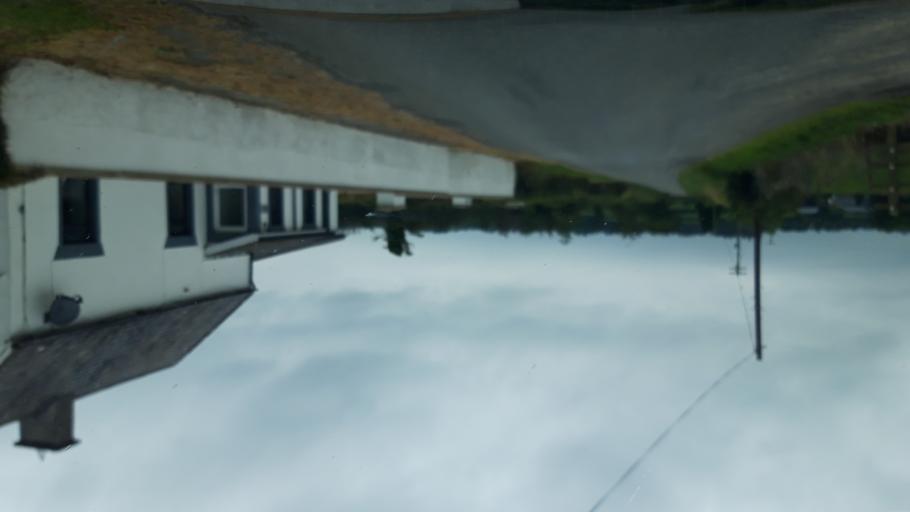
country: IE
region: Leinster
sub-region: Kilkenny
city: Ballyragget
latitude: 52.7074
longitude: -7.4039
